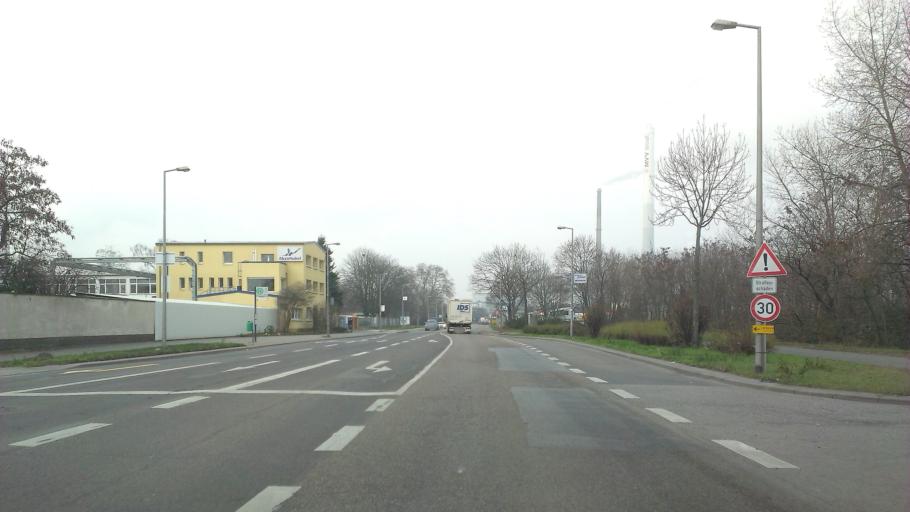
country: DE
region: Baden-Wuerttemberg
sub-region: Karlsruhe Region
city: Mannheim
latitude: 49.5187
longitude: 8.4625
